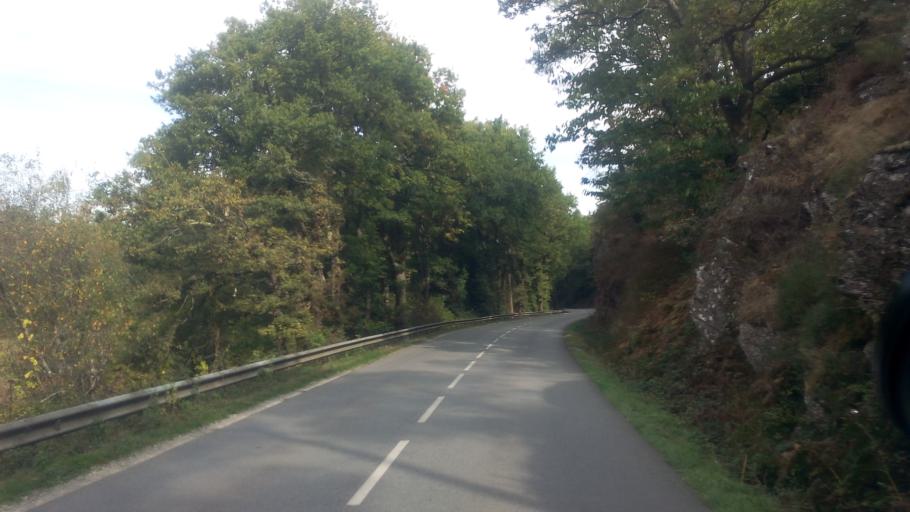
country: FR
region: Brittany
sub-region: Departement du Morbihan
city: La Gacilly
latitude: 47.7562
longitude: -2.1326
